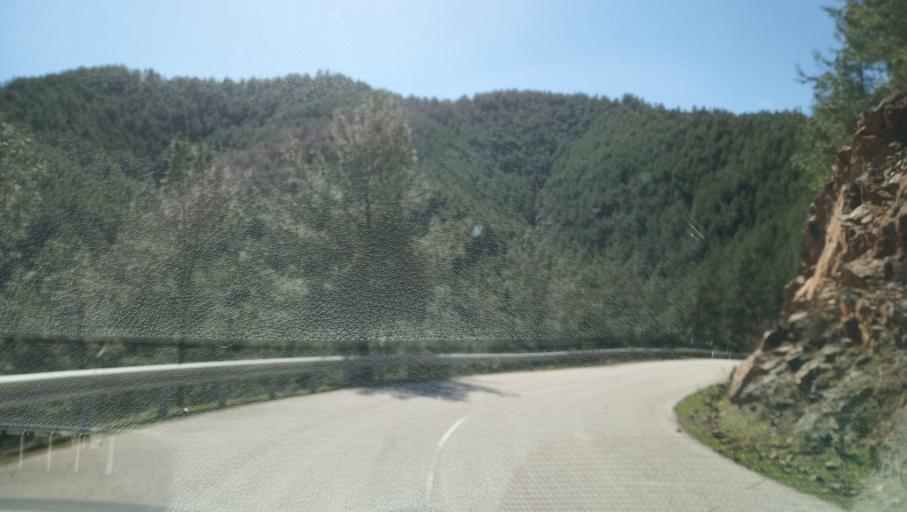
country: CY
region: Lefkosia
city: Lefka
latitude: 35.0699
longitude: 32.7544
